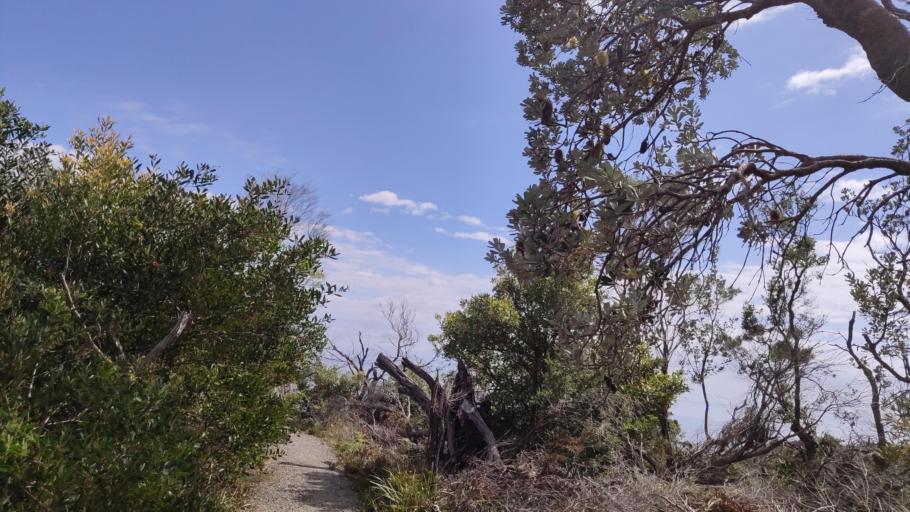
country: AU
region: New South Wales
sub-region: Port Macquarie-Hastings
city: North Haven
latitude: -31.6442
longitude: 152.8407
